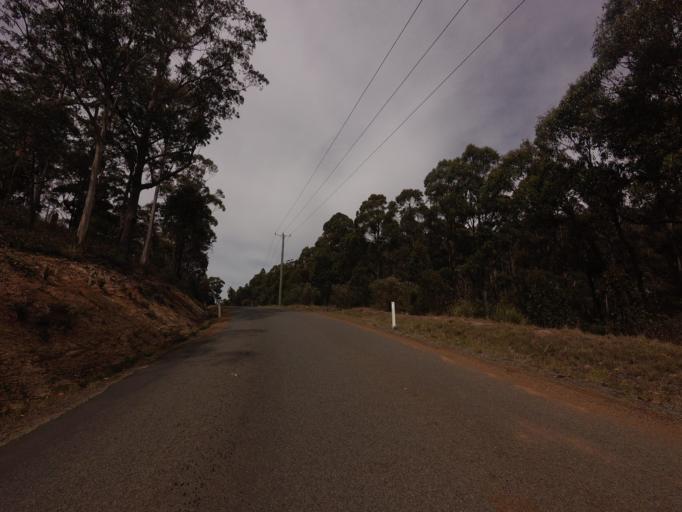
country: AU
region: Tasmania
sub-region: Sorell
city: Sorell
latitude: -42.5818
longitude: 147.5579
